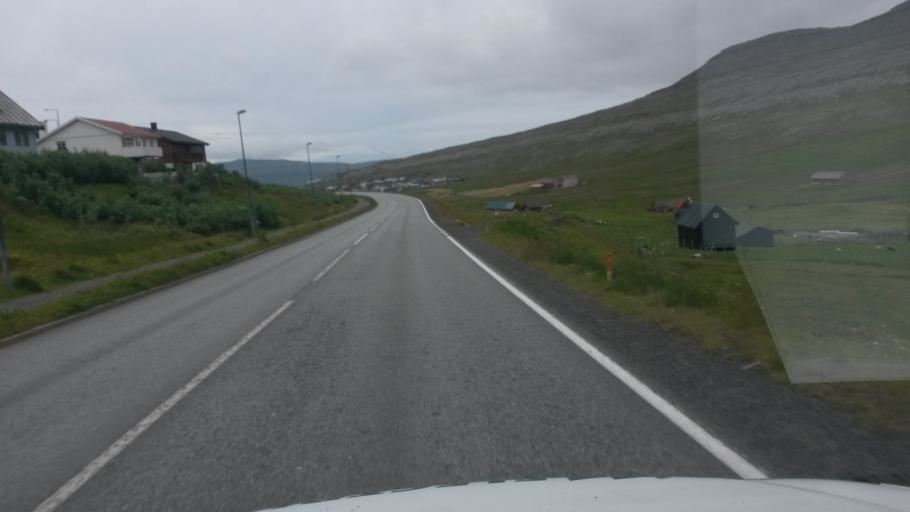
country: FO
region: Streymoy
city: Argir
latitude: 61.9993
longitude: -6.8255
